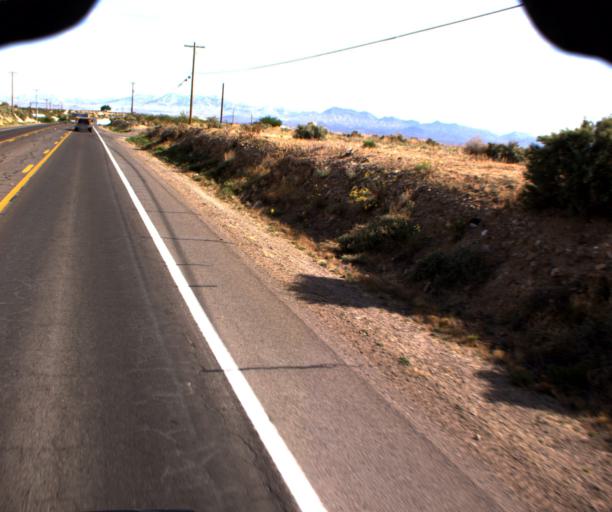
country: US
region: Arizona
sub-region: Graham County
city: Cactus Flat
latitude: 32.7751
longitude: -109.7162
